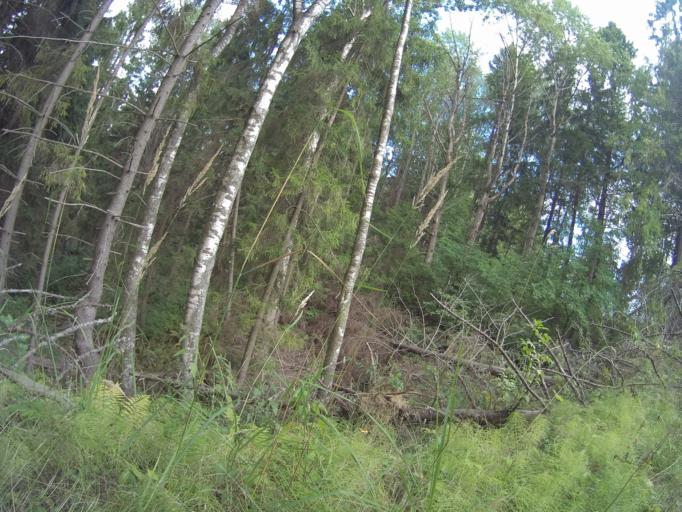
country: RU
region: Vladimir
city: Raduzhnyy
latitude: 56.0140
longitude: 40.3233
